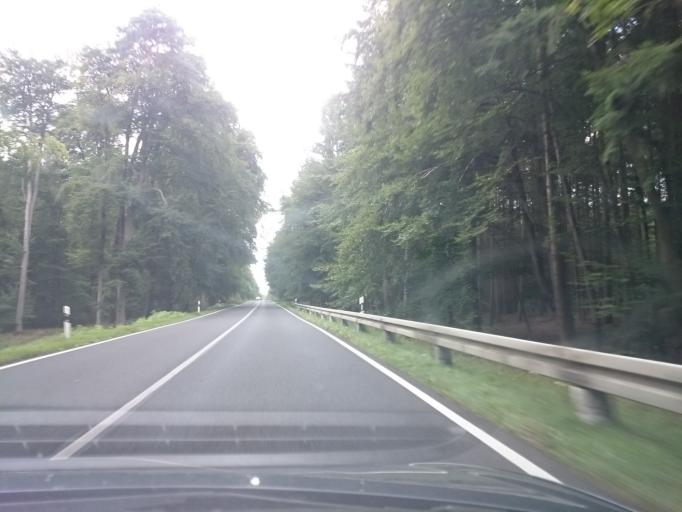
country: DE
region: Mecklenburg-Vorpommern
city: Carpin
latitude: 53.3593
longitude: 13.2229
